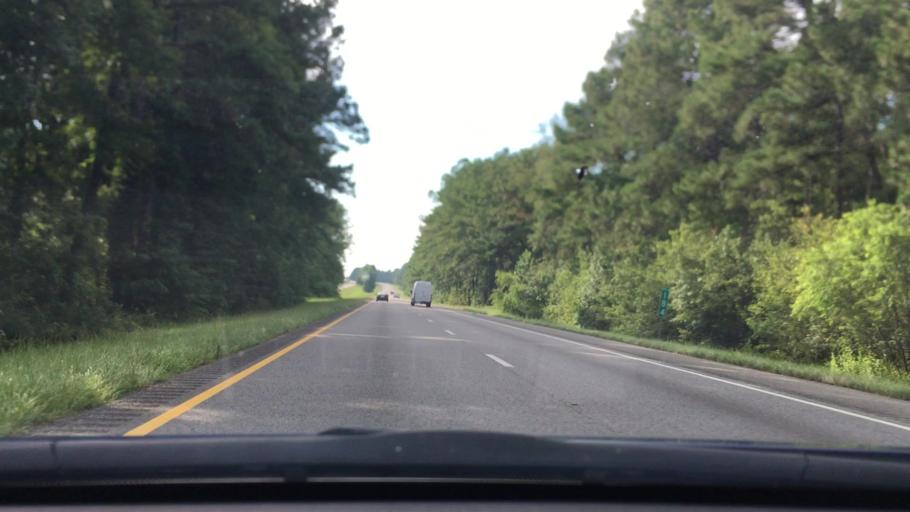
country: US
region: South Carolina
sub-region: Dorchester County
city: Ridgeville
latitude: 33.1632
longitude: -80.3567
